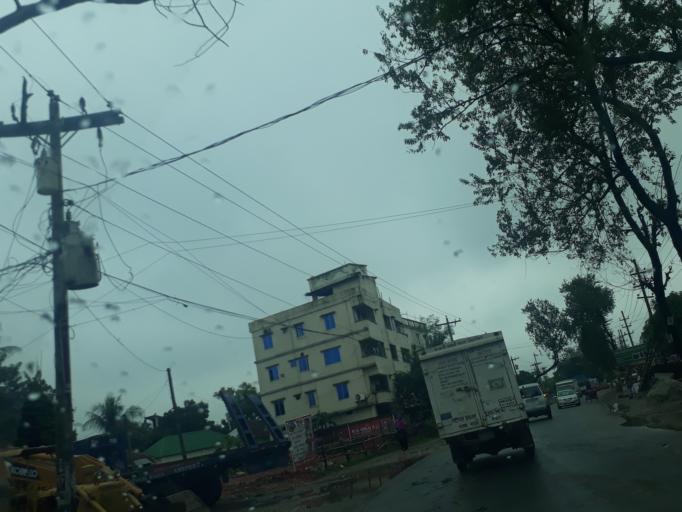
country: BD
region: Dhaka
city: Tungi
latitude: 23.9050
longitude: 90.3239
